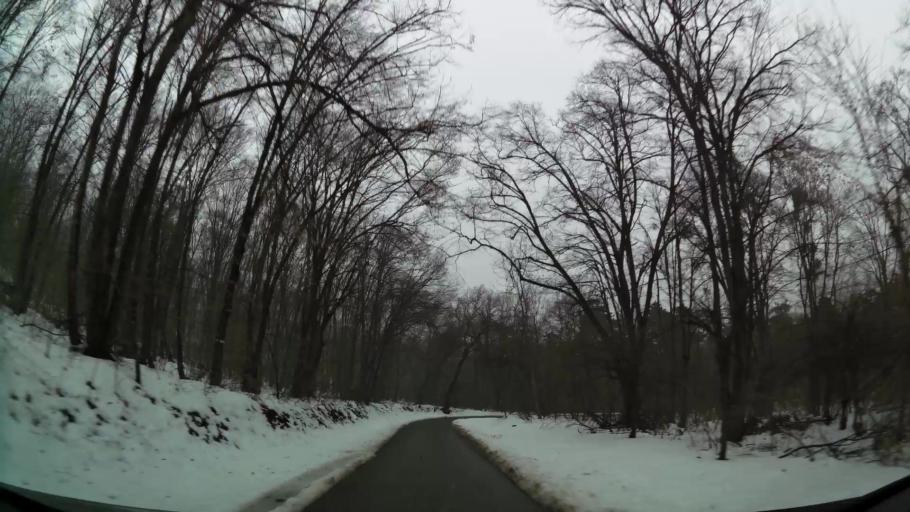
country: RS
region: Central Serbia
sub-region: Belgrade
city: Cukarica
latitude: 44.7782
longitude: 20.4306
